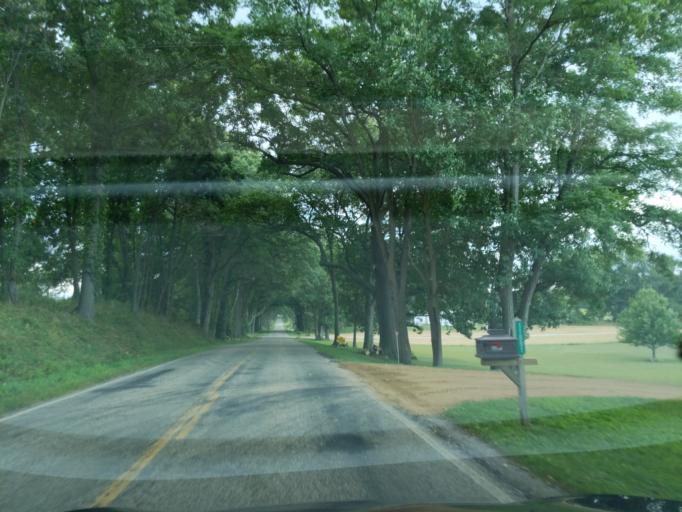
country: US
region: Michigan
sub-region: Eaton County
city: Eaton Rapids
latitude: 42.3785
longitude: -84.6124
